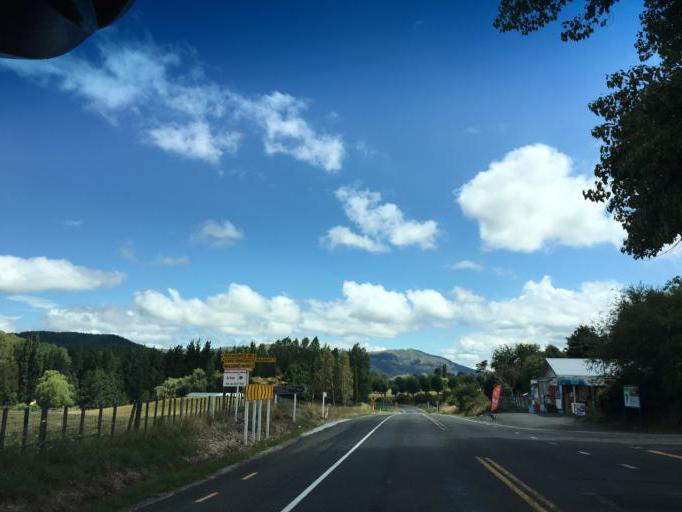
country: NZ
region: Hawke's Bay
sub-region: Napier City
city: Napier
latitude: -39.2040
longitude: 176.8824
